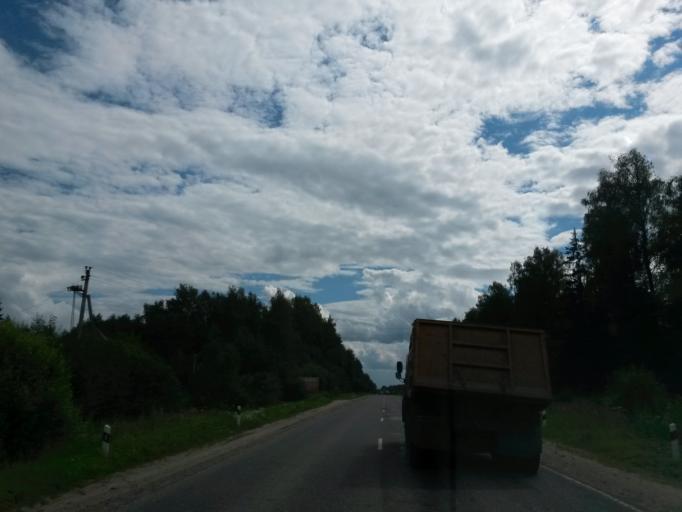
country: RU
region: Ivanovo
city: Novo-Talitsy
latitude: 57.0481
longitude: 40.7377
